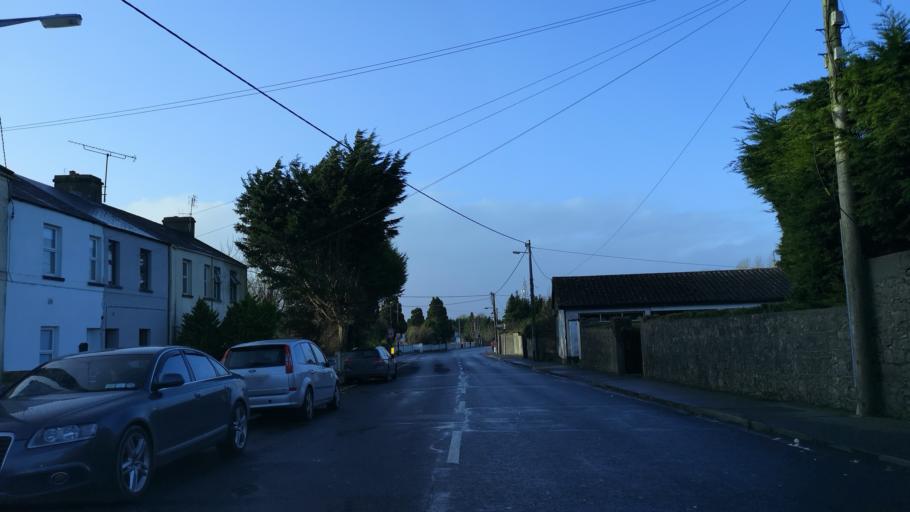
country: IE
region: Connaught
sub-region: County Galway
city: Tuam
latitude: 53.5105
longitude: -8.8441
